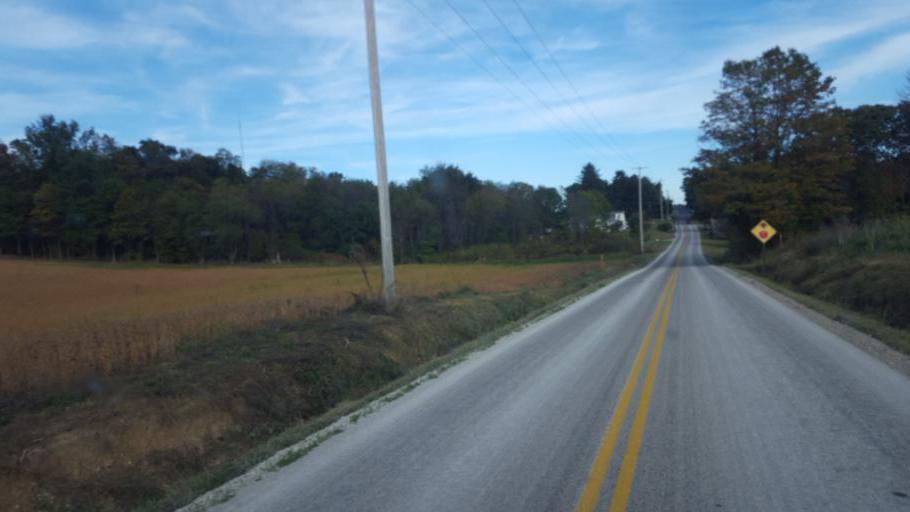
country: US
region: Ohio
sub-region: Richland County
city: Lexington
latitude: 40.5864
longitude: -82.6082
